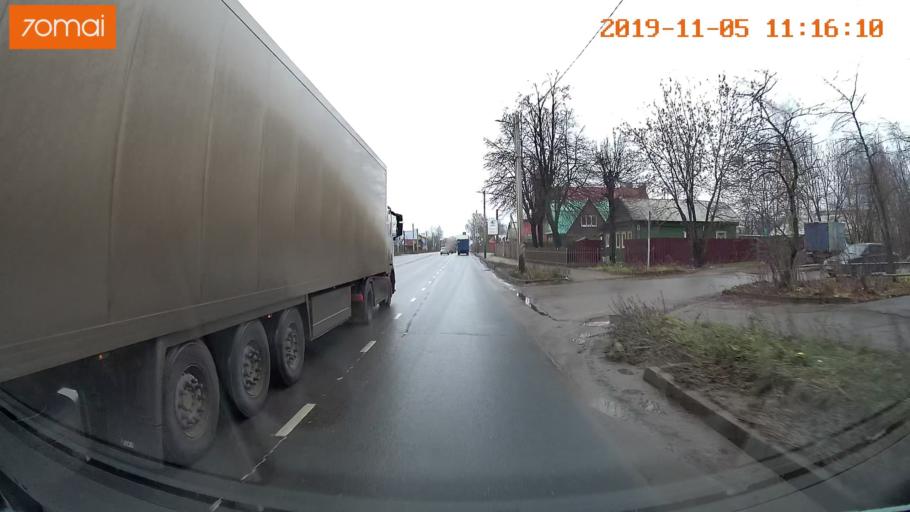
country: RU
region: Ivanovo
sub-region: Gorod Ivanovo
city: Ivanovo
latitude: 56.9825
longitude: 40.9536
